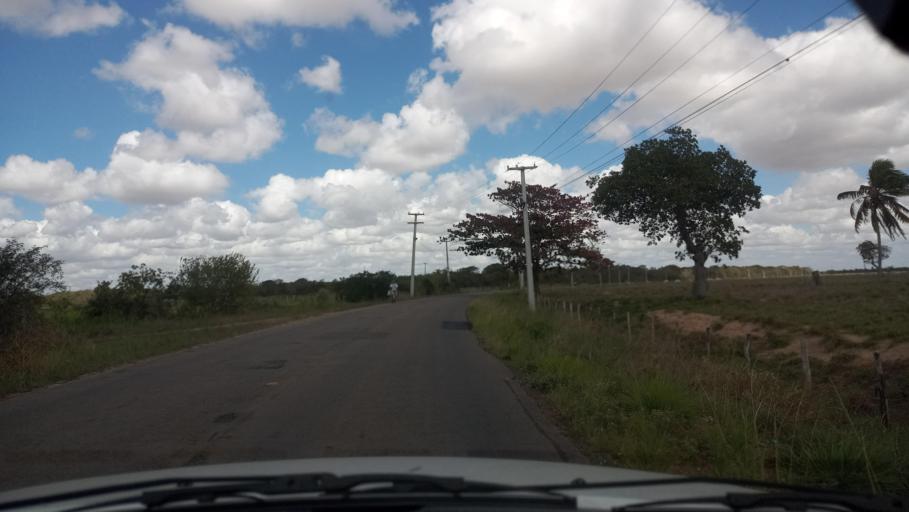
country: BR
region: Rio Grande do Norte
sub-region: Brejinho
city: Brejinho
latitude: -6.0414
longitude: -35.4054
